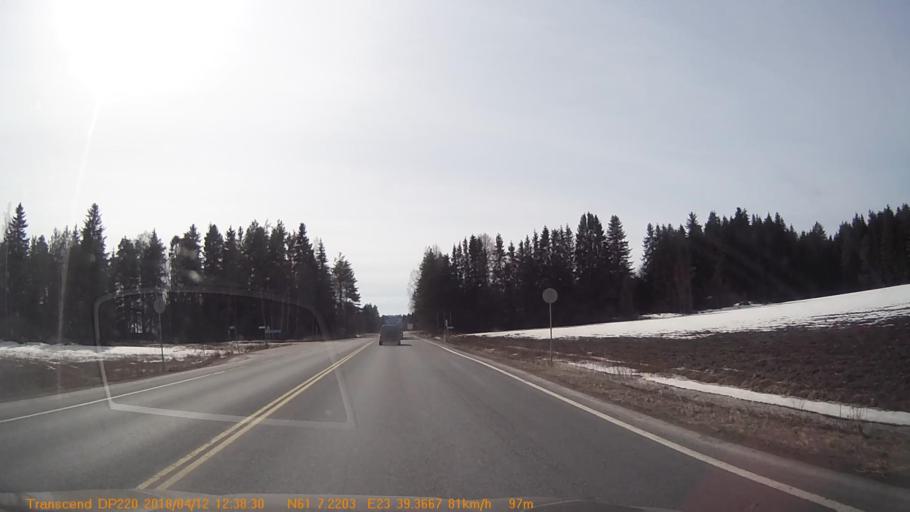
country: FI
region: Pirkanmaa
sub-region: Etelae-Pirkanmaa
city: Kylmaekoski
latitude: 61.1204
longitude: 23.6562
